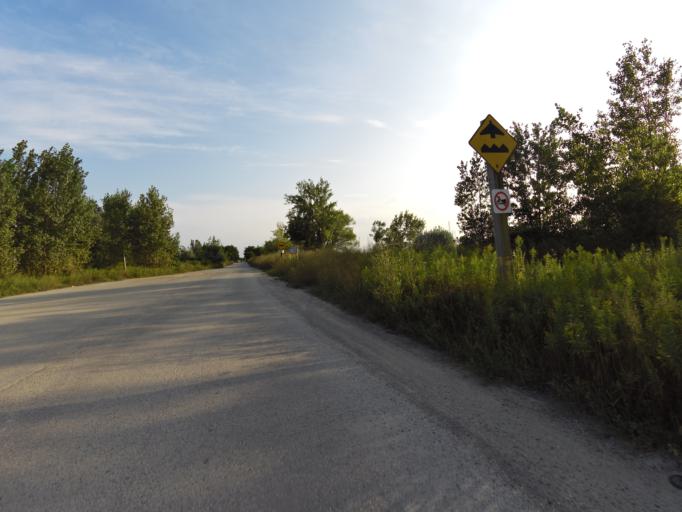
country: CA
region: Ontario
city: Toronto
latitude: 43.6453
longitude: -79.3213
